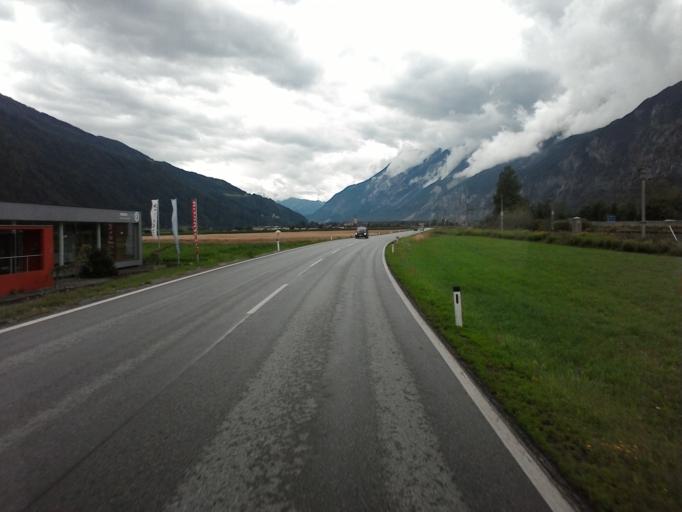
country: AT
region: Tyrol
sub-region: Politischer Bezirk Imst
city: Motz
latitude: 47.2723
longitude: 10.9547
